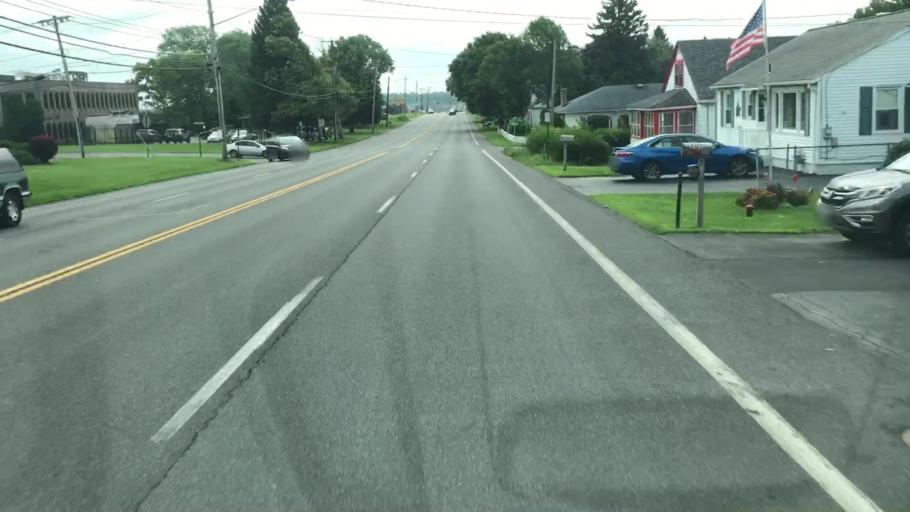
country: US
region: New York
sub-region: Onondaga County
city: Galeville
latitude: 43.0952
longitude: -76.1758
